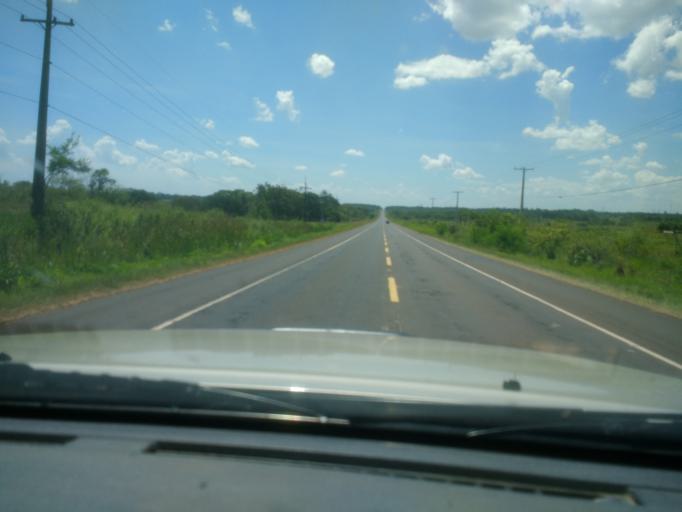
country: PY
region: San Pedro
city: Itacurubi del Rosario
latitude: -24.5126
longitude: -56.8527
